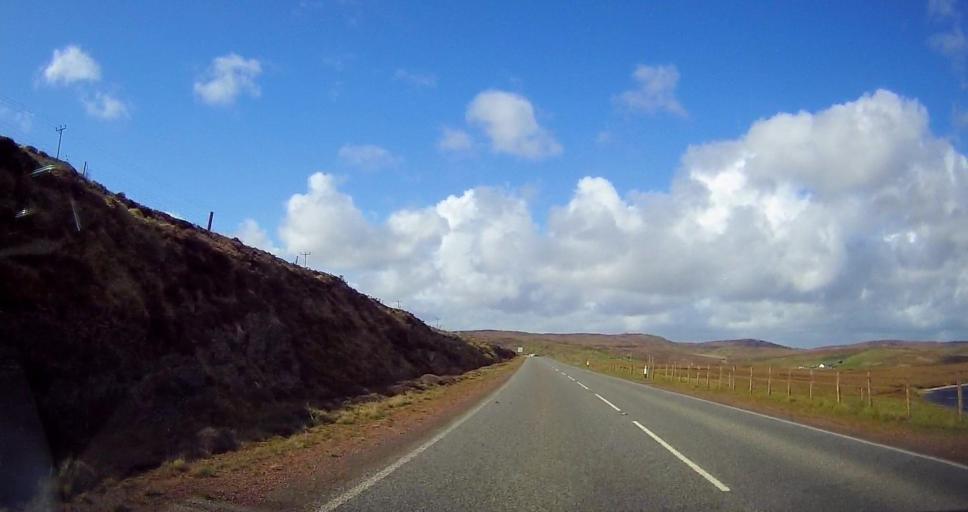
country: GB
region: Scotland
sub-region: Shetland Islands
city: Lerwick
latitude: 60.2598
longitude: -1.2222
